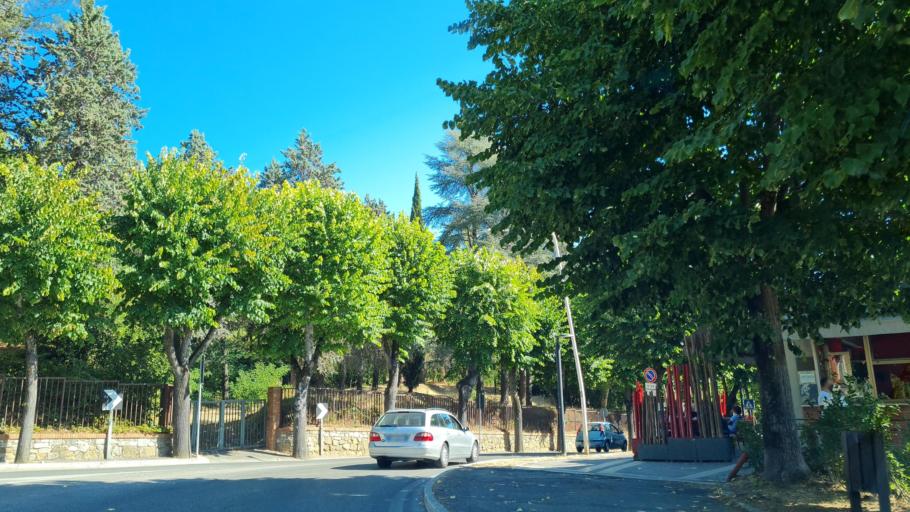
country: IT
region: Tuscany
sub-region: Provincia di Siena
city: Chianciano Terme
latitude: 43.0563
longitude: 11.8224
